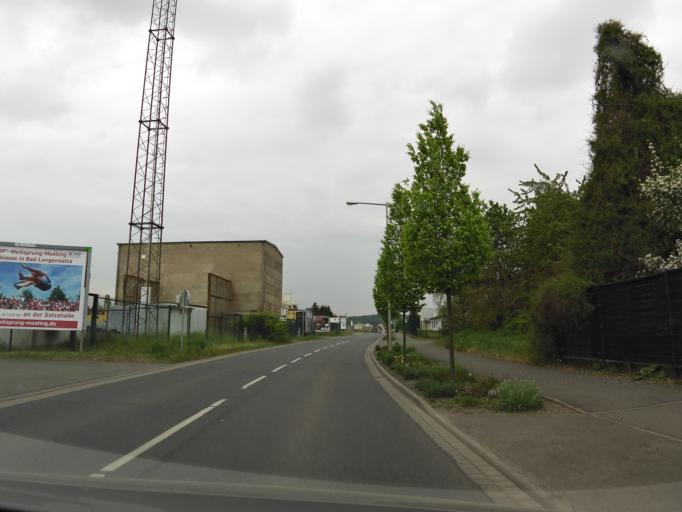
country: DE
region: Thuringia
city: Gotha
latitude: 50.9533
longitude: 10.7272
